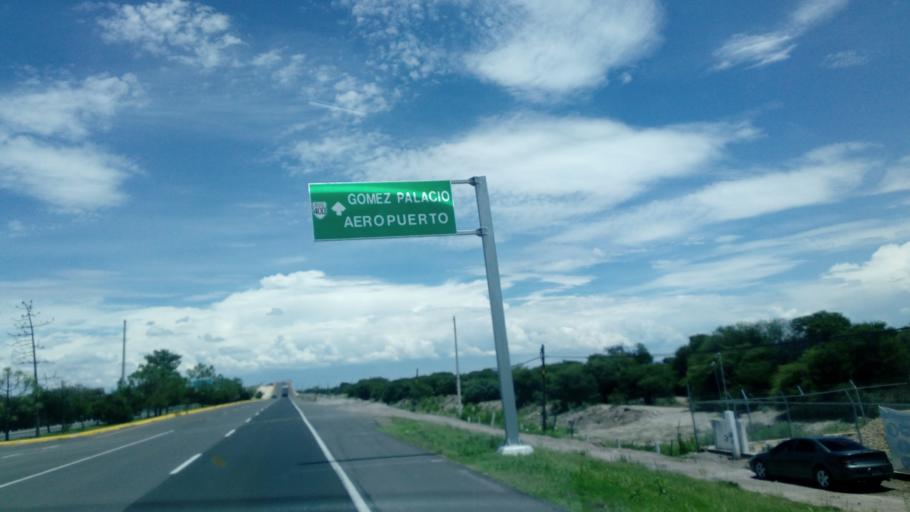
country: MX
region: Durango
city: Victoria de Durango
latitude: 24.1084
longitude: -104.5559
